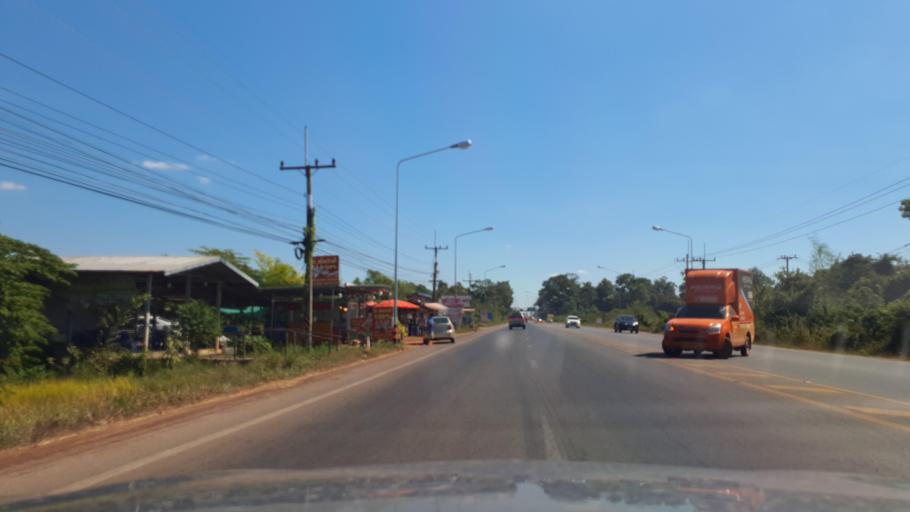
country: TH
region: Sakon Nakhon
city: Sakon Nakhon
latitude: 17.0877
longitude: 104.1821
